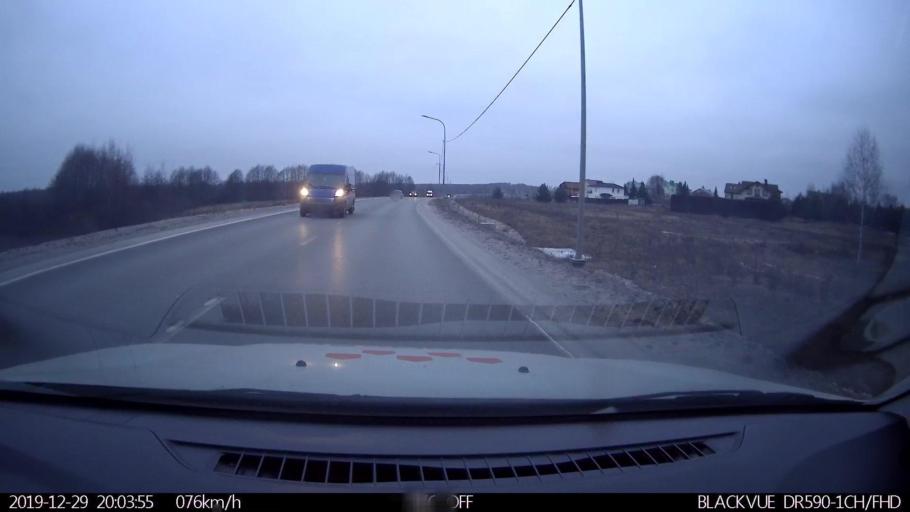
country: RU
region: Nizjnij Novgorod
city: Nizhniy Novgorod
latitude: 56.3777
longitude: 44.0117
